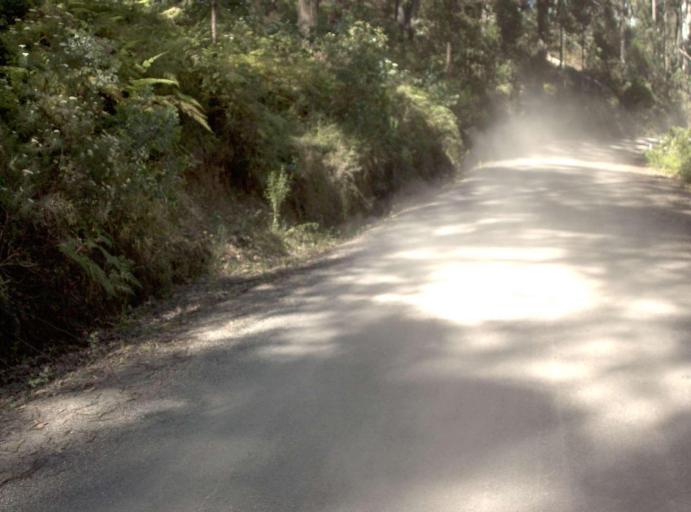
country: AU
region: New South Wales
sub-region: Bombala
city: Bombala
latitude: -37.2510
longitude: 148.7406
